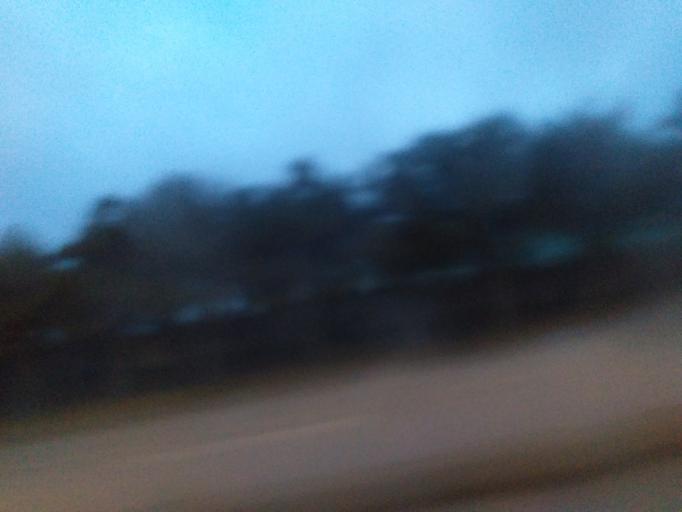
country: TR
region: Ankara
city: Ankara
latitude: 39.9597
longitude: 32.8229
